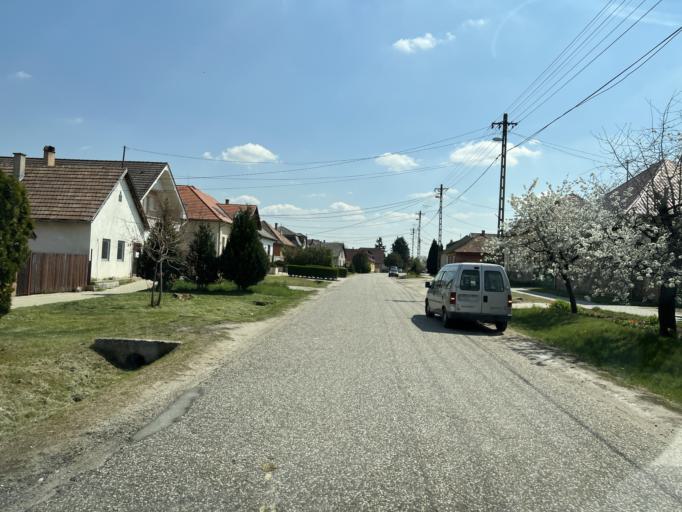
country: HU
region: Pest
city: Orbottyan
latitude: 47.6594
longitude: 19.2331
